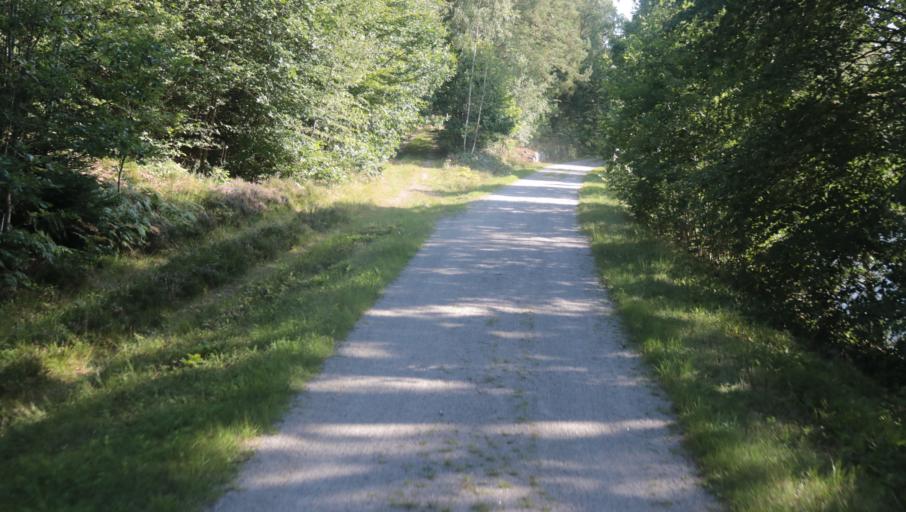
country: SE
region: Blekinge
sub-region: Karlshamns Kommun
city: Svangsta
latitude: 56.3714
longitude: 14.6829
